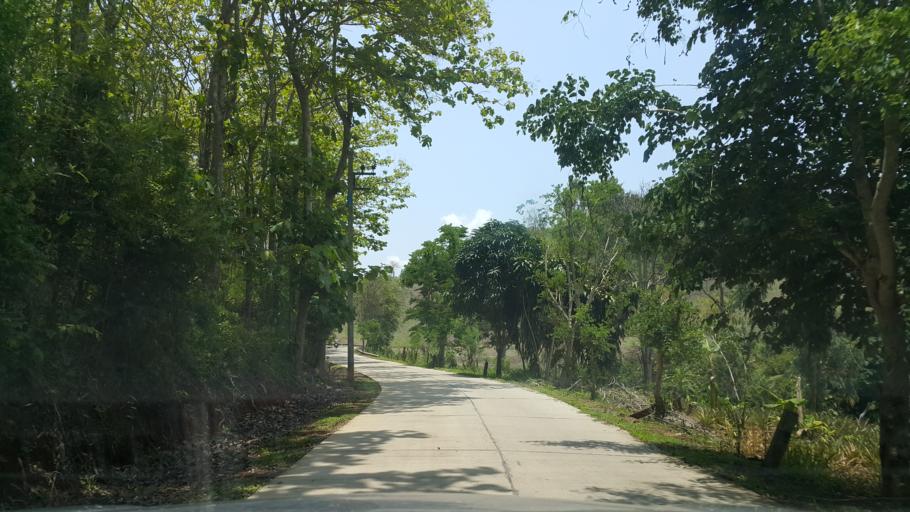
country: TH
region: Chiang Rai
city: Chiang Rai
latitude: 19.9761
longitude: 99.7445
